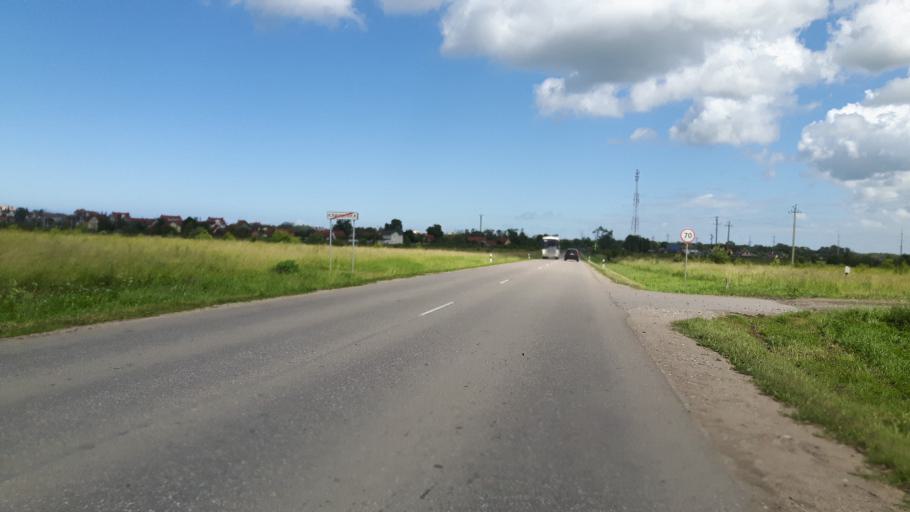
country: RU
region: Kaliningrad
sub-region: Zelenogradskiy Rayon
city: Zelenogradsk
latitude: 54.9405
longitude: 20.4562
